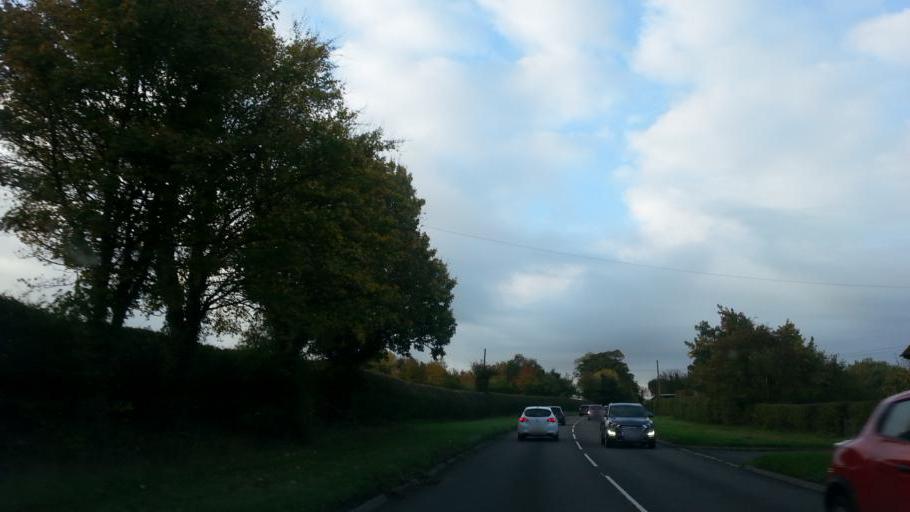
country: GB
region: England
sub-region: Staffordshire
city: Fazeley
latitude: 52.6087
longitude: -1.7476
